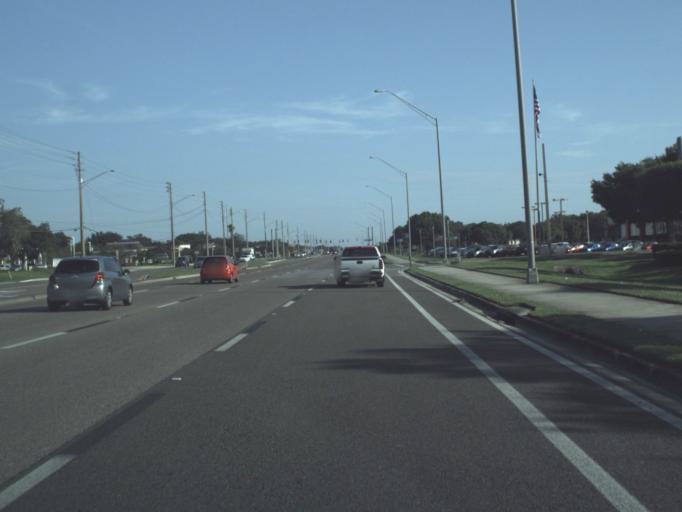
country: US
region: Florida
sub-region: Polk County
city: Gibsonia
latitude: 28.0962
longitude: -81.9736
